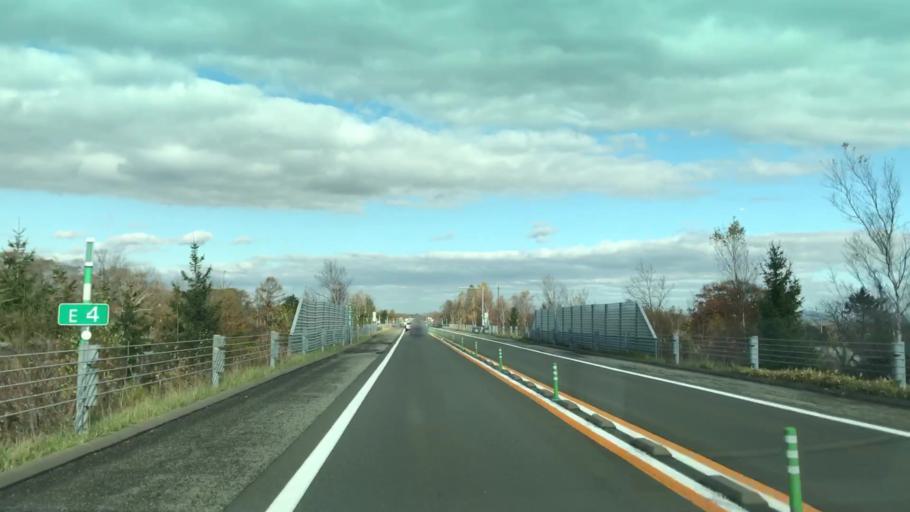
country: JP
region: Hokkaido
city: Chitose
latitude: 42.8726
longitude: 141.6143
